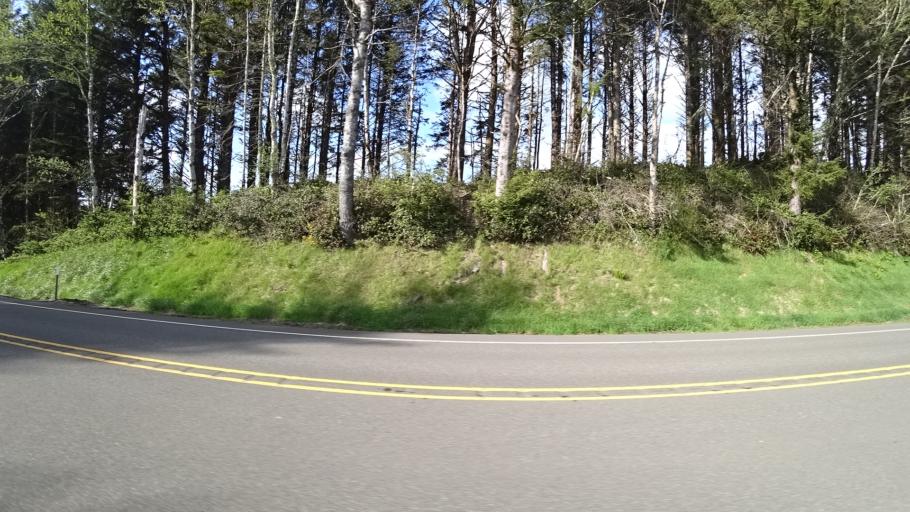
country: US
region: Oregon
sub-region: Douglas County
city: Reedsport
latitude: 43.7707
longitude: -124.1412
